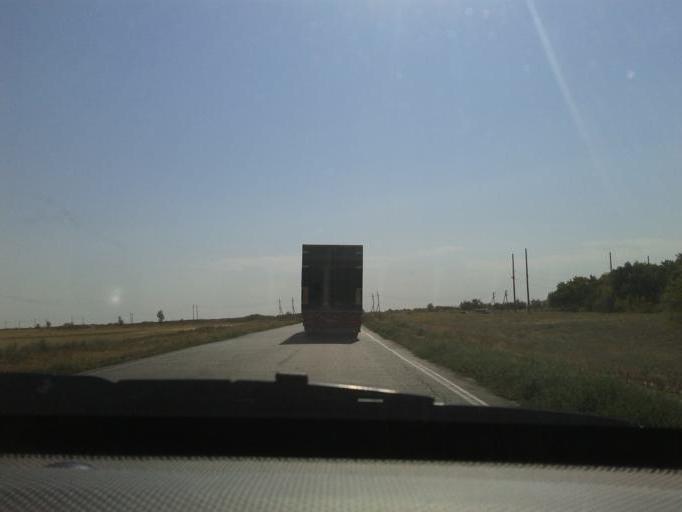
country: RU
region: Astrakhan
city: Znamensk
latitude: 48.6193
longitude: 45.5470
